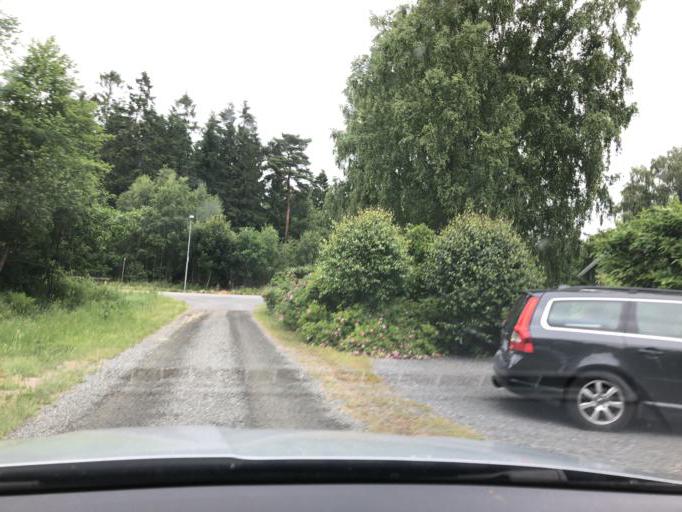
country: SE
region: Blekinge
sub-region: Solvesborgs Kommun
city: Soelvesborg
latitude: 56.1420
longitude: 14.5962
